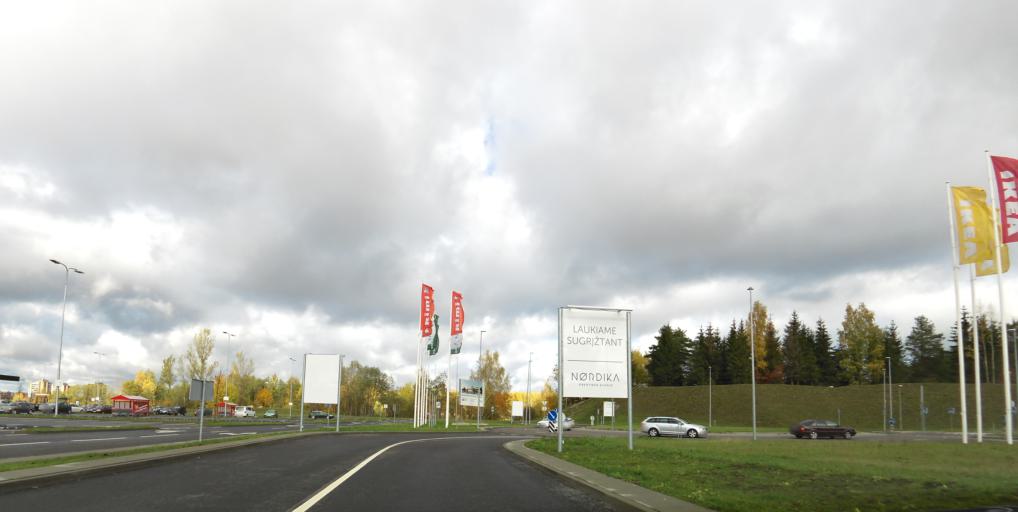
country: LT
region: Vilnius County
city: Naujamiestis
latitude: 54.6527
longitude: 25.2790
